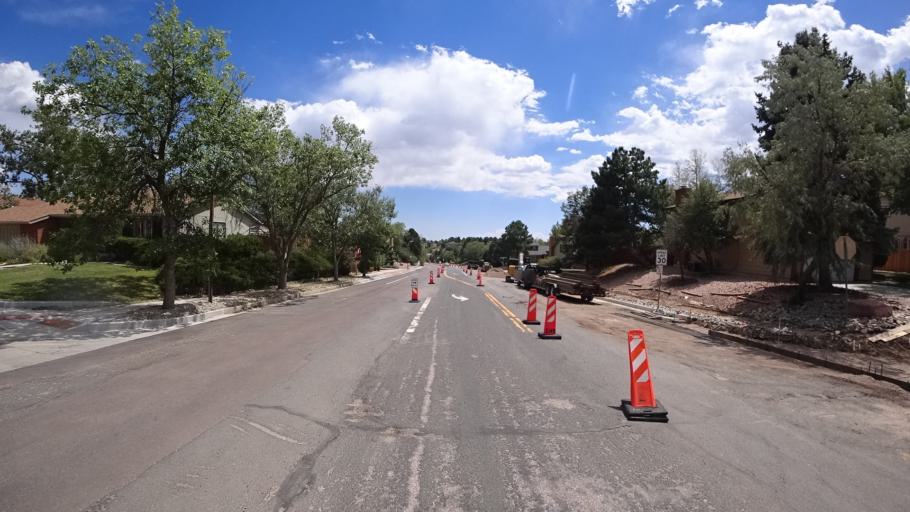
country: US
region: Colorado
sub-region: El Paso County
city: Stratmoor
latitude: 38.7873
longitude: -104.8180
